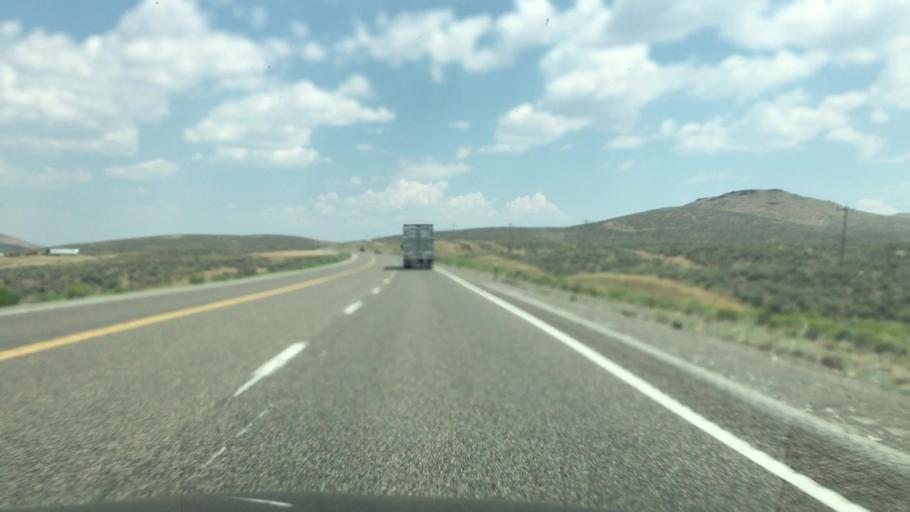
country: US
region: Nevada
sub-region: Elko County
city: Wells
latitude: 41.1752
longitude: -114.8791
